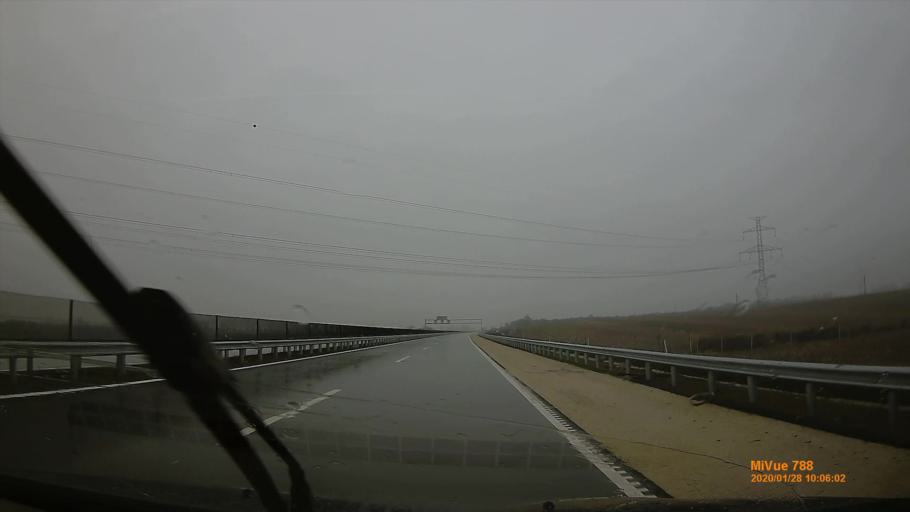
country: HU
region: Pest
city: Pilis
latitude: 47.2814
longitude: 19.5895
